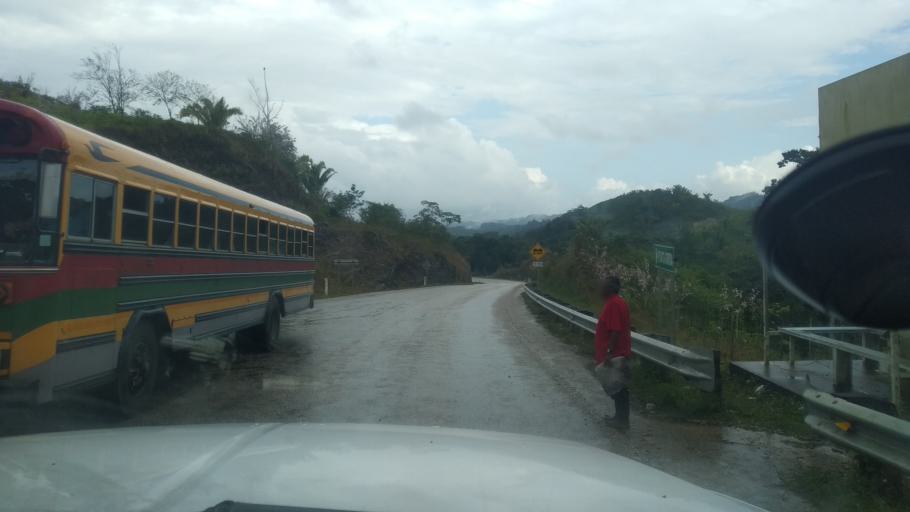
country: GT
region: Peten
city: San Luis
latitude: 16.1864
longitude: -89.1929
